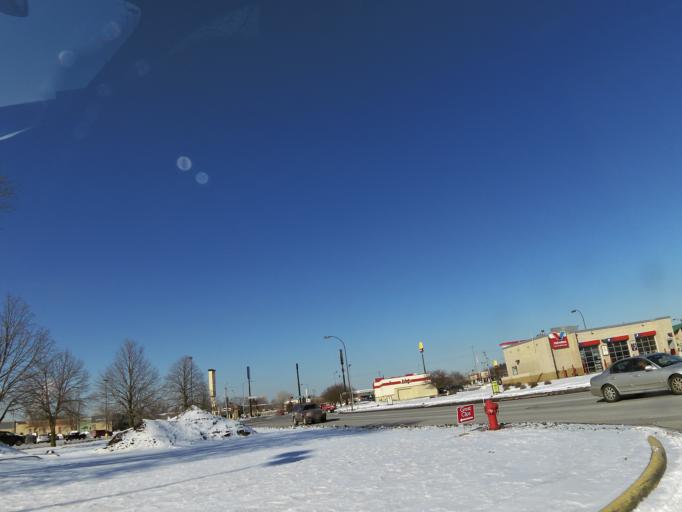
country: US
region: Wisconsin
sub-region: Saint Croix County
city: Hudson
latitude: 44.9594
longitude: -92.7235
